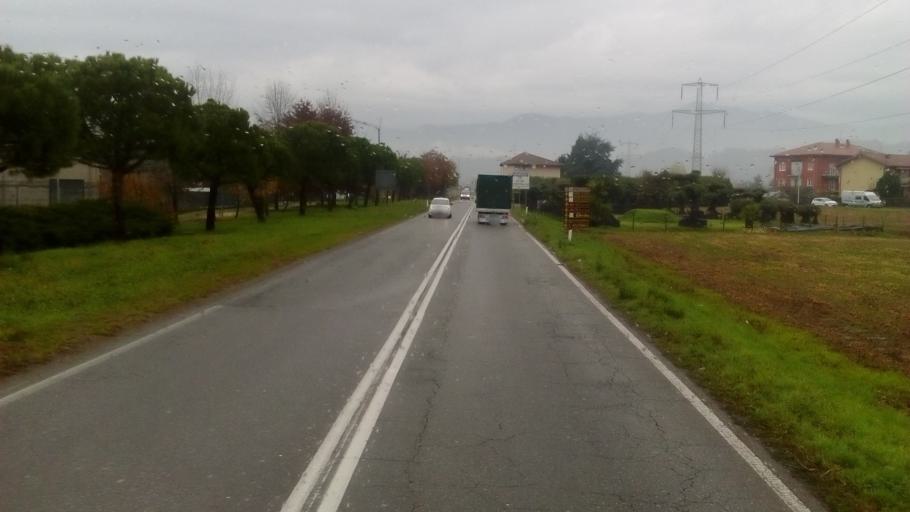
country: IT
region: Lombardy
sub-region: Provincia di Bergamo
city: Mozzo
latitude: 45.7076
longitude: 9.6068
